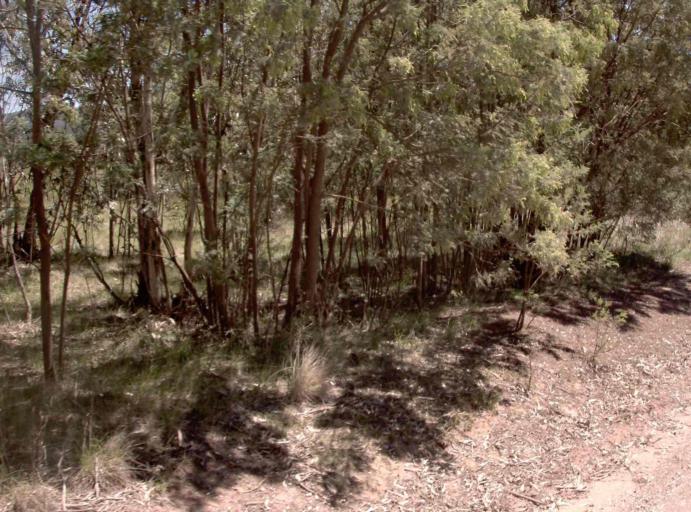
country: AU
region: New South Wales
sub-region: Snowy River
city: Jindabyne
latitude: -37.0804
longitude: 148.2596
